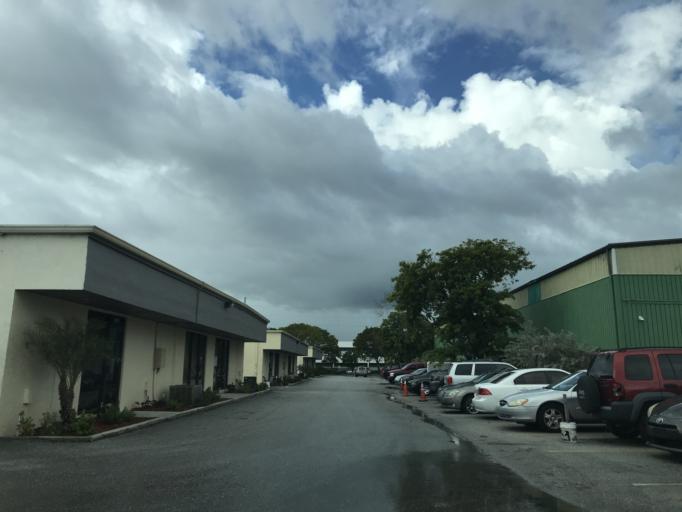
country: US
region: Florida
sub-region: Palm Beach County
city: Delray Beach
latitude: 26.4570
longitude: -80.0914
